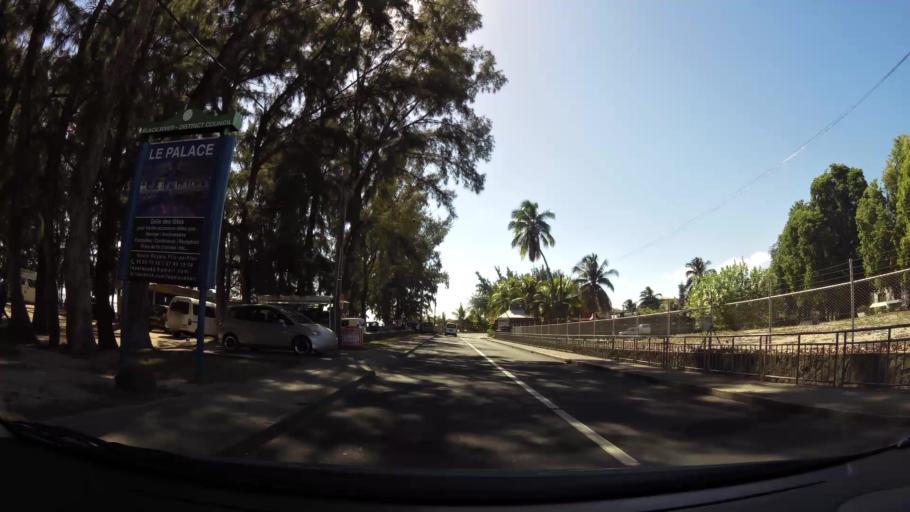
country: MU
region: Black River
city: Flic en Flac
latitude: -20.2805
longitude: 57.3662
